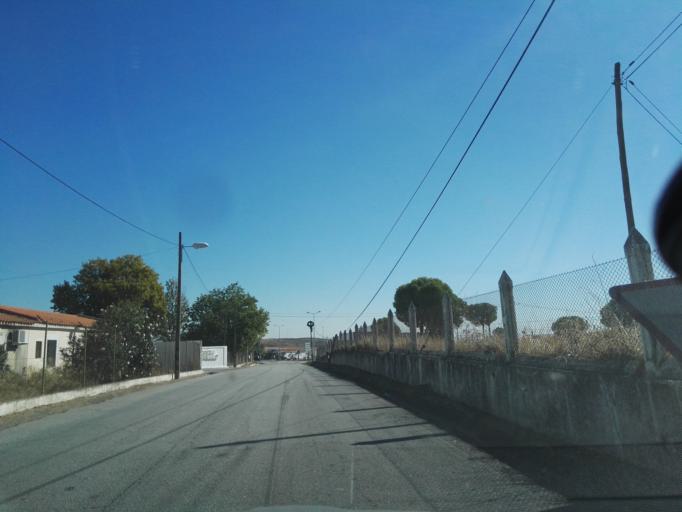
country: PT
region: Portalegre
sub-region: Elvas
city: Elvas
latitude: 38.8881
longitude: -7.1304
